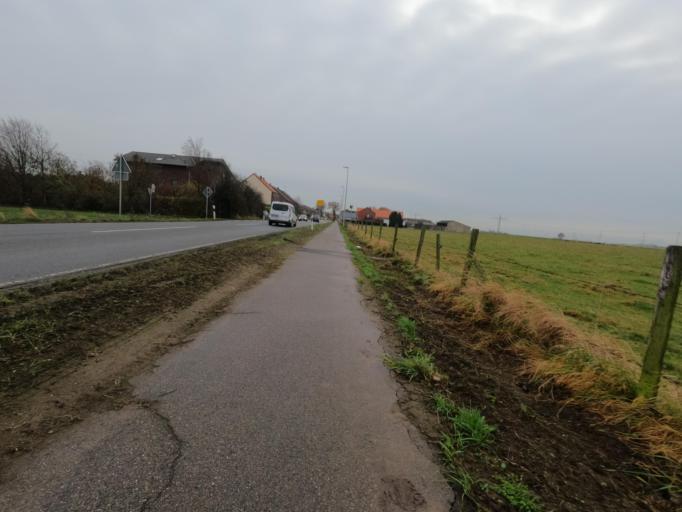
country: DE
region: North Rhine-Westphalia
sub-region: Regierungsbezirk Koln
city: Heinsberg
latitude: 51.0514
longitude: 6.1084
